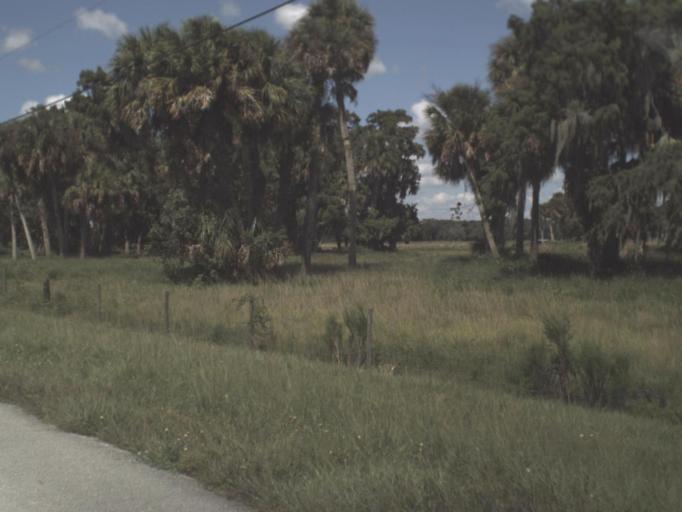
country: US
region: Florida
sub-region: Okeechobee County
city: Taylor Creek
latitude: 27.1764
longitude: -80.7293
